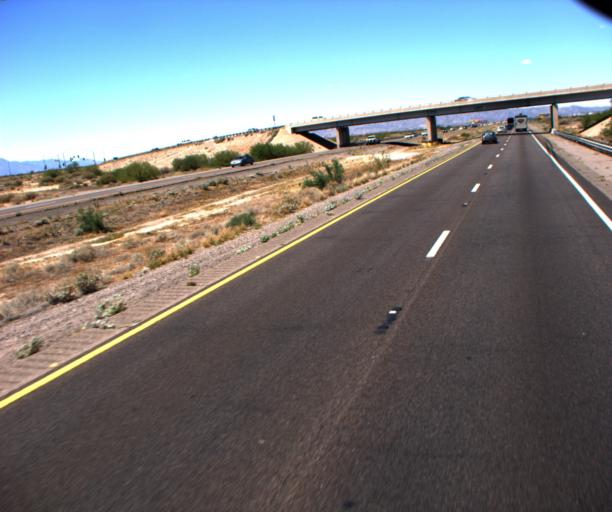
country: US
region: Arizona
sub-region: Maricopa County
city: Sun Lakes
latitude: 33.2183
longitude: -111.9192
